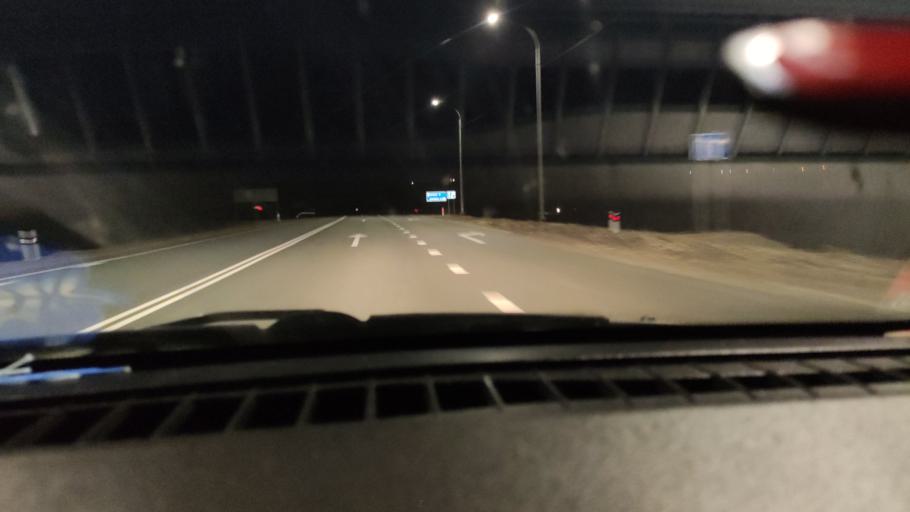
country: RU
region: Saratov
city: Shikhany
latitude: 52.1279
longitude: 47.2368
